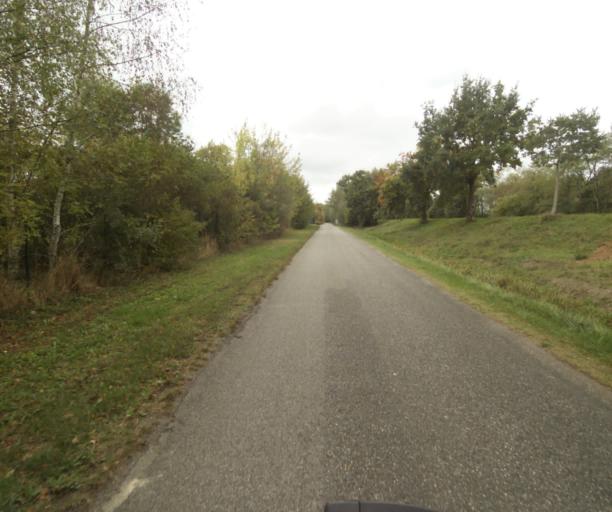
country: FR
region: Midi-Pyrenees
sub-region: Departement du Tarn-et-Garonne
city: Montech
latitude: 43.9667
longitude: 1.2408
